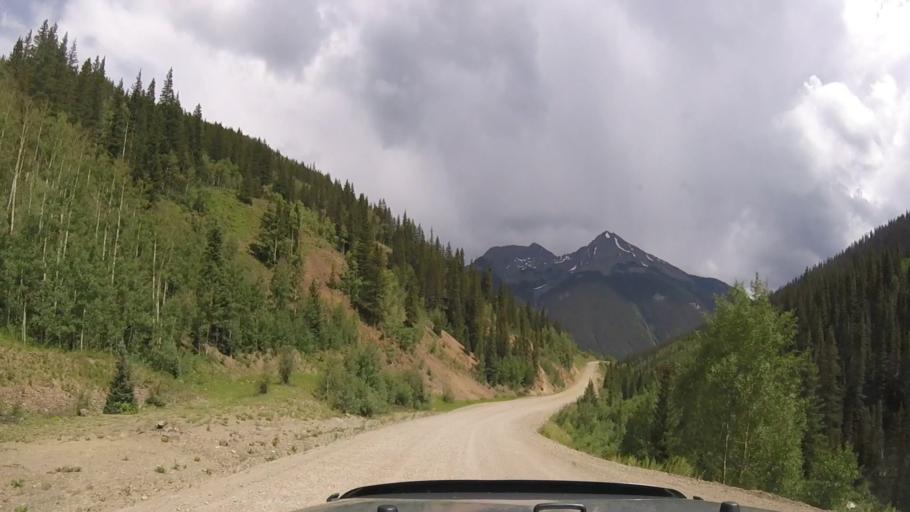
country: US
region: Colorado
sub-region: San Juan County
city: Silverton
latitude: 37.8266
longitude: -107.6683
